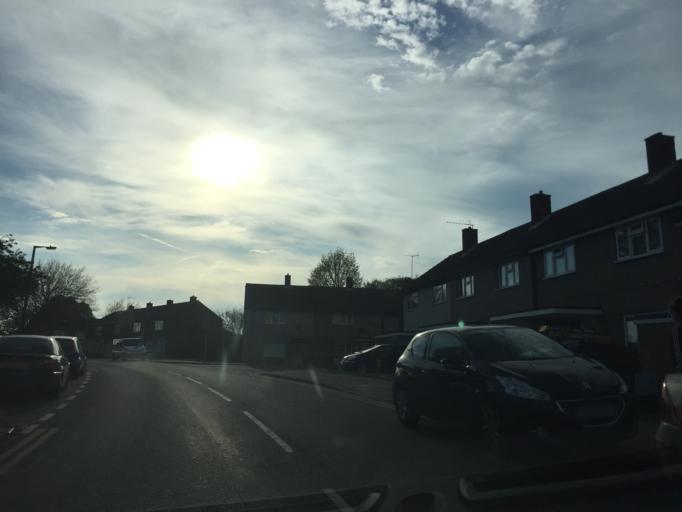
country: GB
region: England
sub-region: Essex
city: Harlow
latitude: 51.7637
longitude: 0.1189
